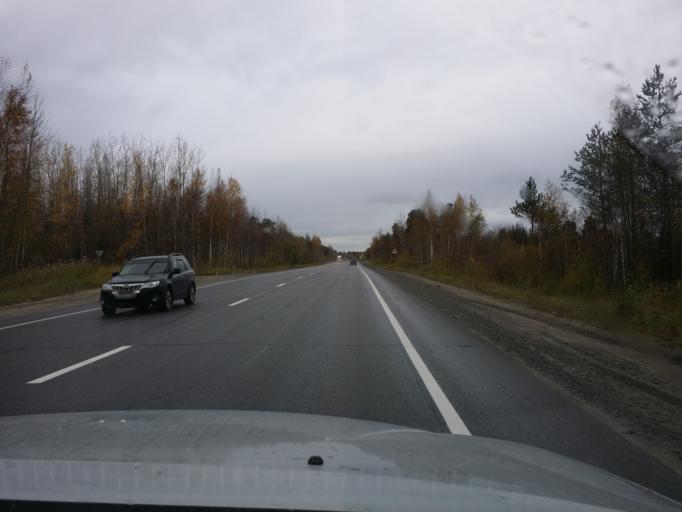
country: RU
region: Khanty-Mansiyskiy Avtonomnyy Okrug
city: Megion
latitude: 61.1047
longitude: 76.0455
